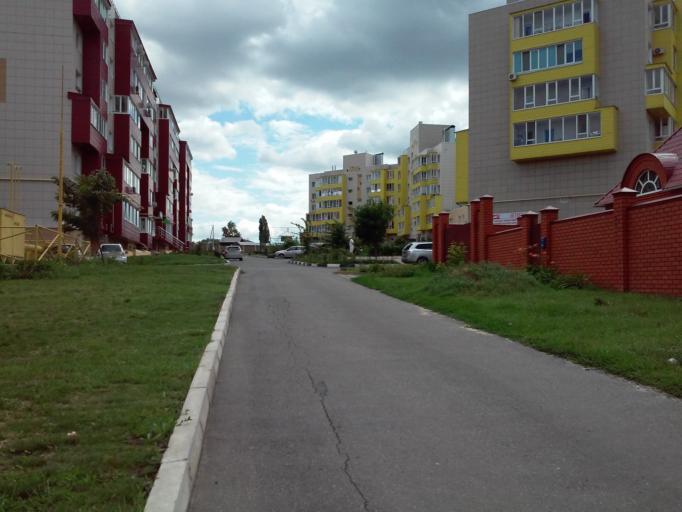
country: RU
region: Belgorod
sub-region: Belgorodskiy Rayon
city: Belgorod
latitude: 50.5359
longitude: 36.5760
